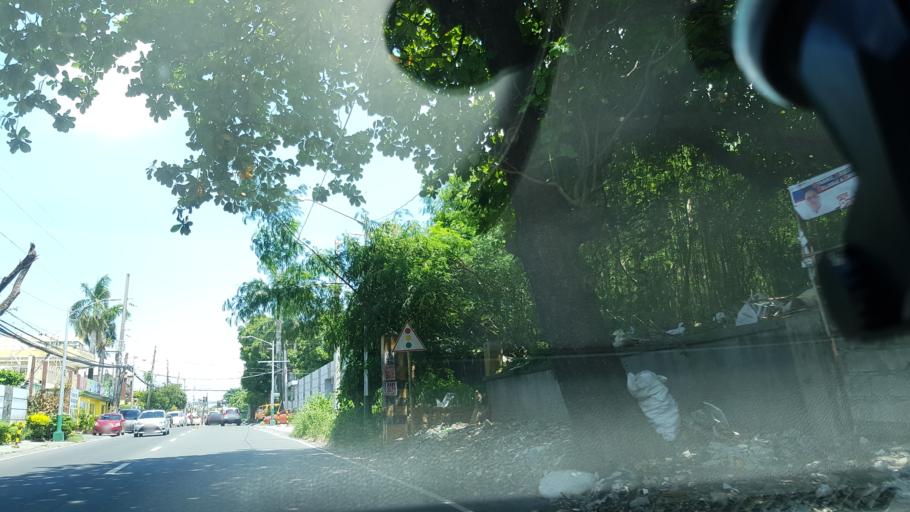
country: PH
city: Sambayanihan People's Village
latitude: 14.4464
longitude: 121.0184
